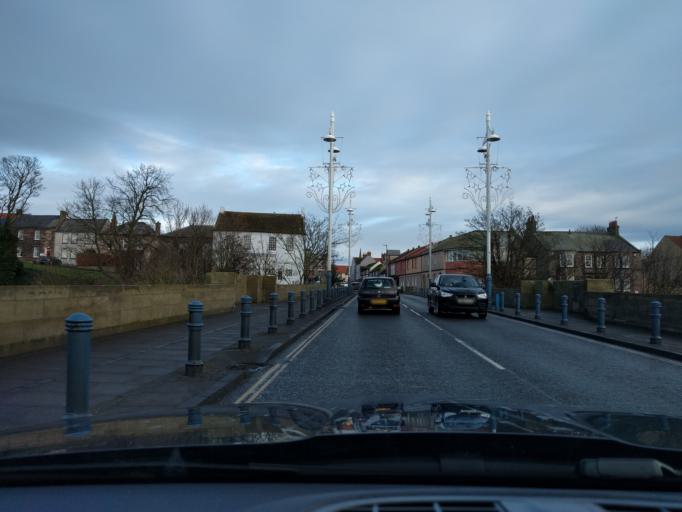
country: GB
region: England
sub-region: Northumberland
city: Berwick-Upon-Tweed
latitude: 55.7693
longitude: -2.0074
